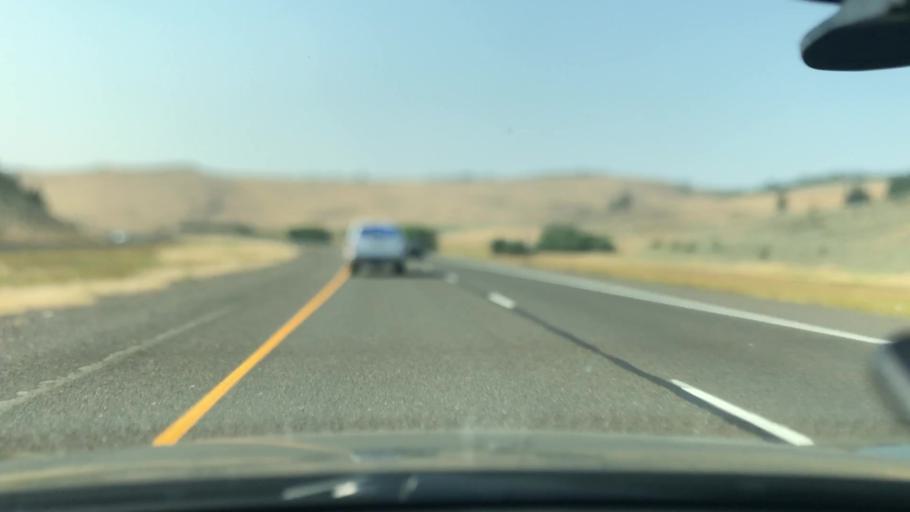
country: US
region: Oregon
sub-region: Union County
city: Union
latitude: 45.1662
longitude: -117.9646
